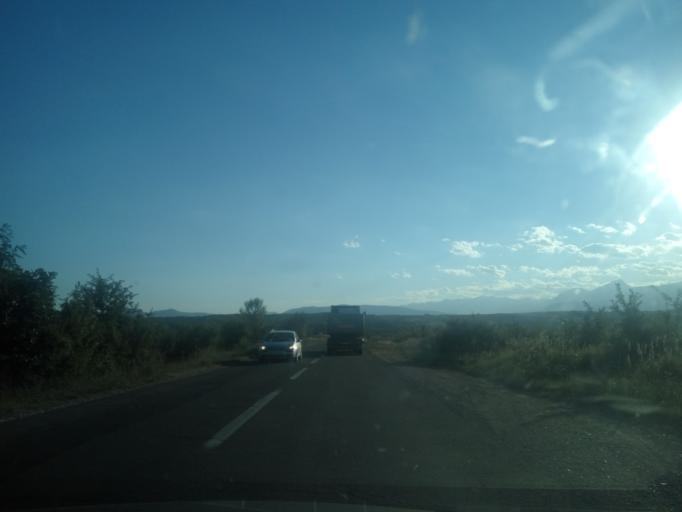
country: XK
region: Gjakova
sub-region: Komuna e Gjakoves
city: Gjakove
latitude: 42.4373
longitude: 20.4786
